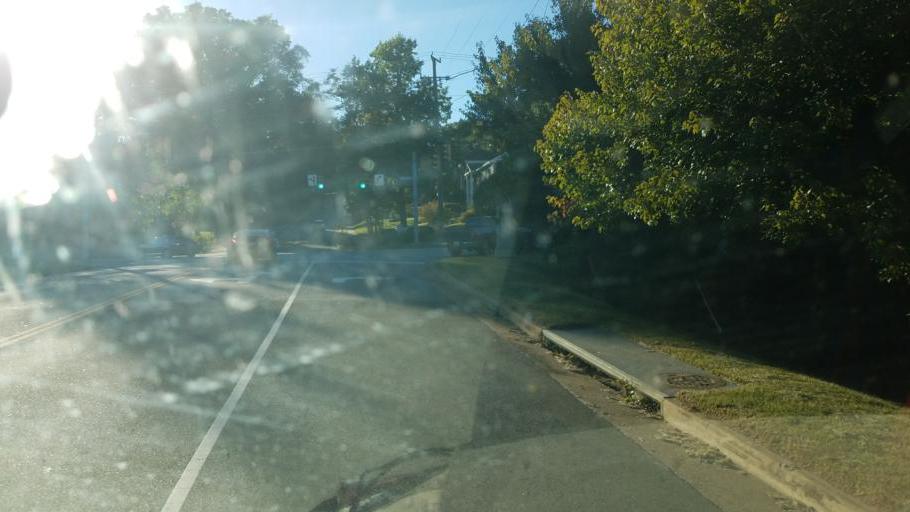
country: US
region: Virginia
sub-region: Fairfax County
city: Belle Haven
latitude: 38.7810
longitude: -77.0617
